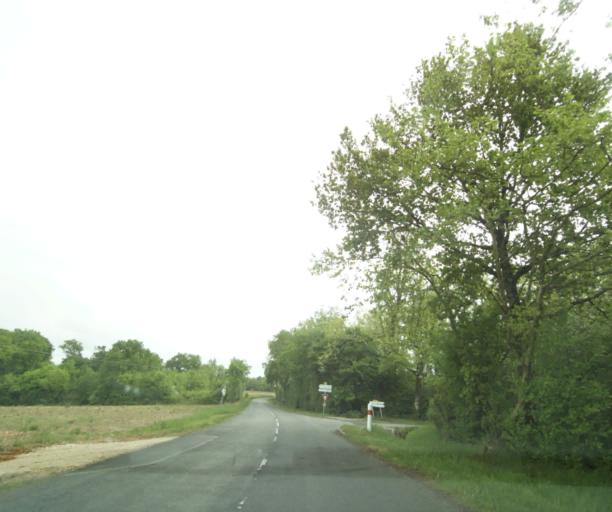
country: FR
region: Poitou-Charentes
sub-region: Departement de la Charente-Maritime
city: Chaniers
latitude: 45.7623
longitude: -0.5309
